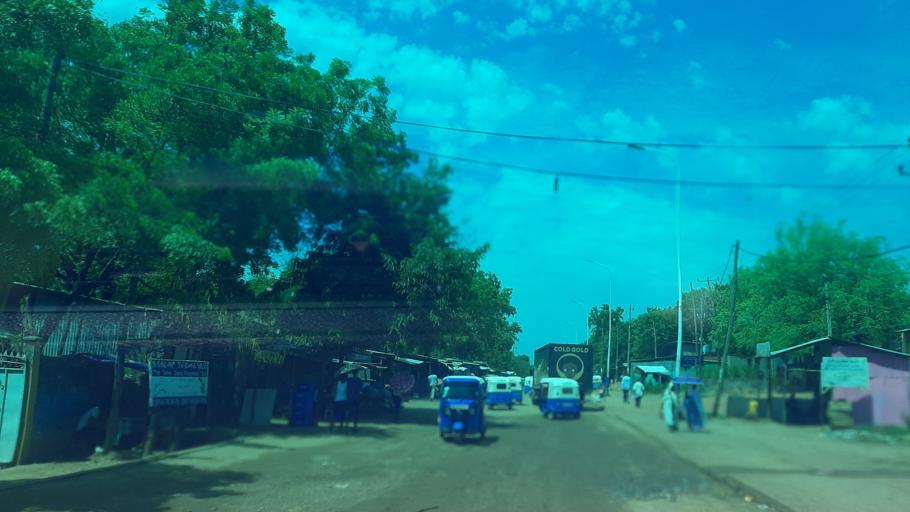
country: ET
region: Gambela
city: Gambela
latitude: 8.2364
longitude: 34.5834
